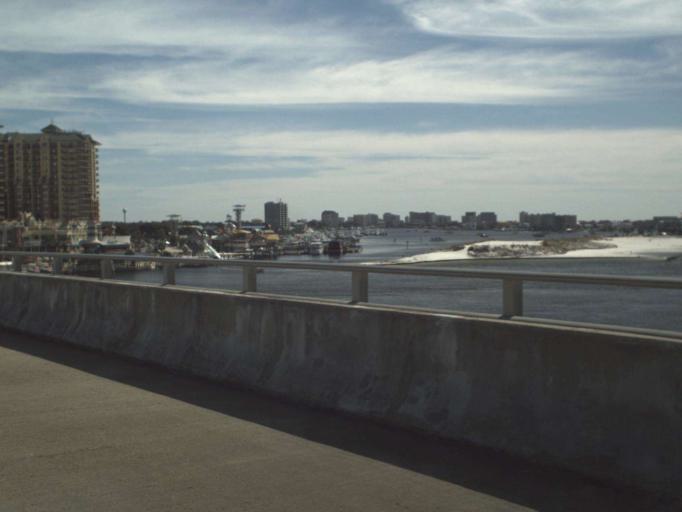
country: US
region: Florida
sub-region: Okaloosa County
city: Destin
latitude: 30.3939
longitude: -86.5168
